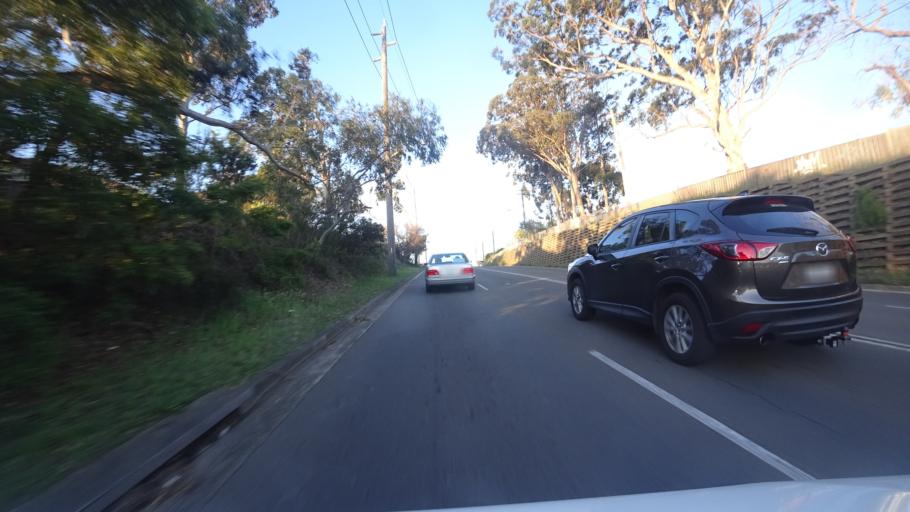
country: AU
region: New South Wales
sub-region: Ryde
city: North Ryde
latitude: -33.8021
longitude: 151.1158
